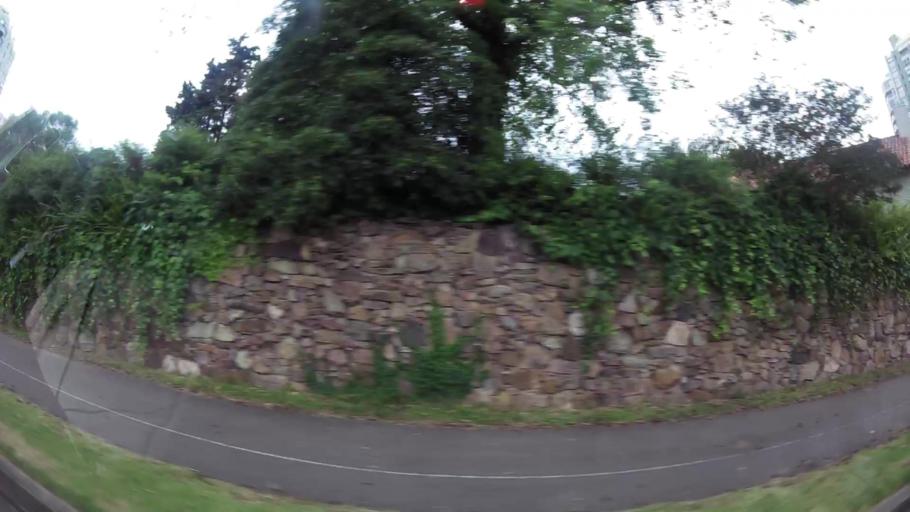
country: UY
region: Maldonado
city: Maldonado
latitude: -34.9220
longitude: -54.9531
